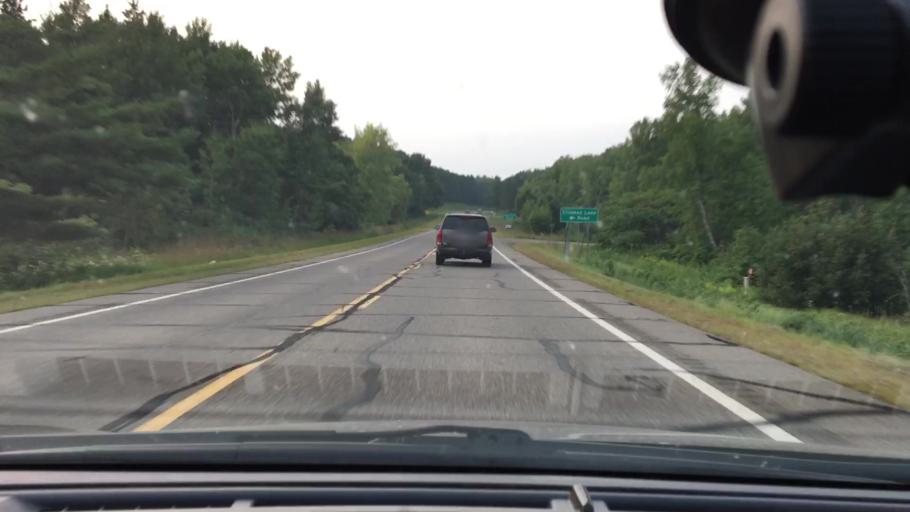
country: US
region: Minnesota
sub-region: Crow Wing County
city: Crosby
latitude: 46.3962
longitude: -93.8777
